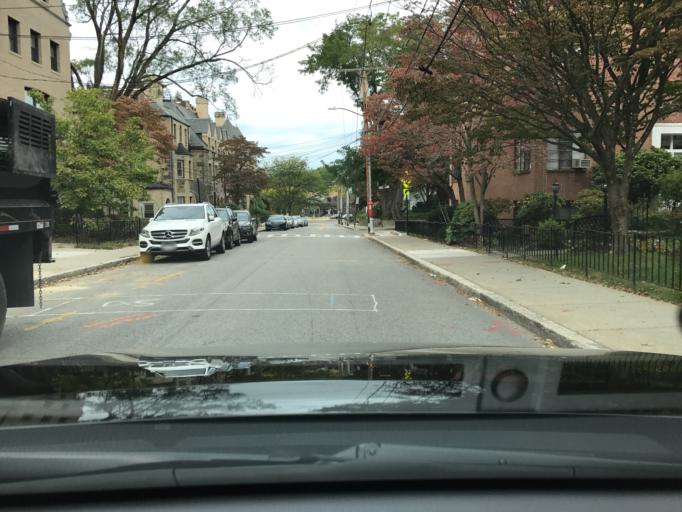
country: US
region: Massachusetts
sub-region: Norfolk County
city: Brookline
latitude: 42.3370
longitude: -71.1383
